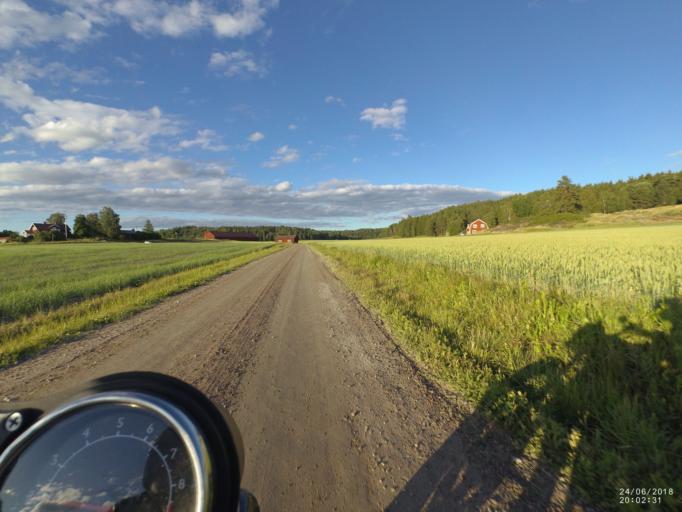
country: SE
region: Soedermanland
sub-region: Nykopings Kommun
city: Nykoping
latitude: 58.7950
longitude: 17.1206
